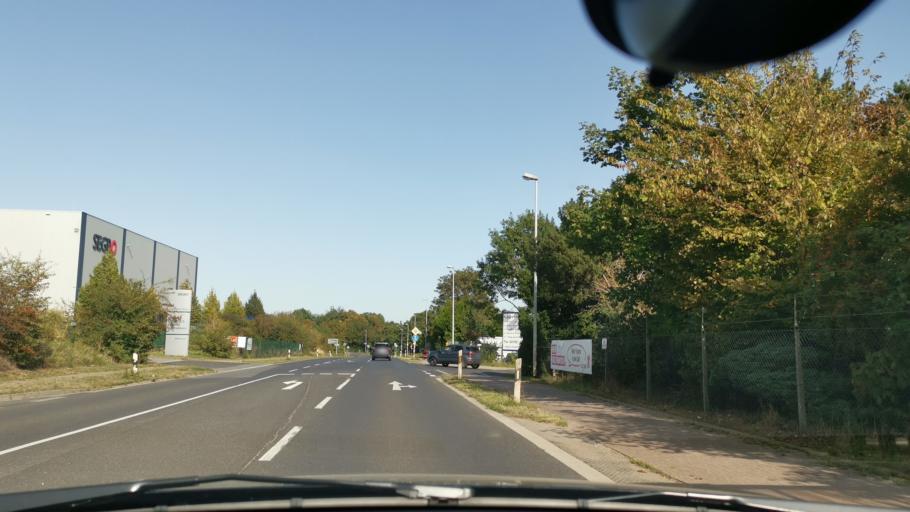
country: DE
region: North Rhine-Westphalia
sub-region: Regierungsbezirk Dusseldorf
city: Neubrueck
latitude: 51.1353
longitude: 6.6181
